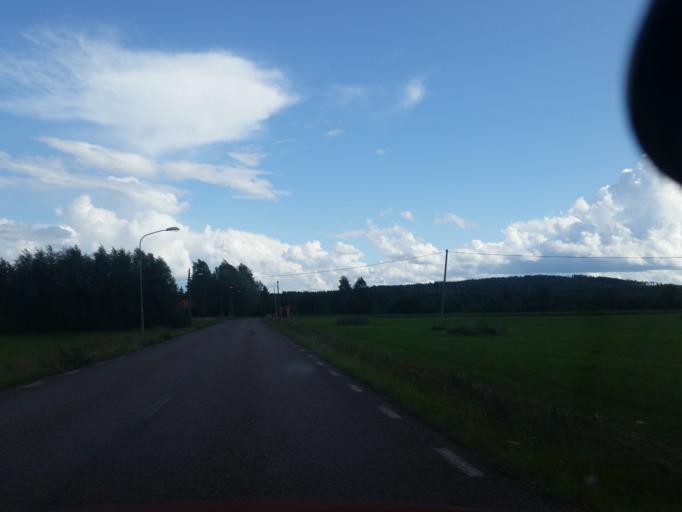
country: SE
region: Dalarna
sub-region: Leksand Municipality
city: Smedby
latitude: 60.6821
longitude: 15.1076
